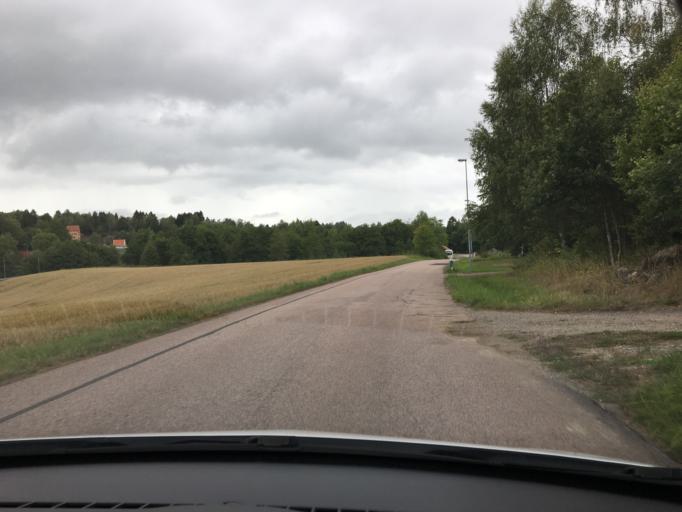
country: SE
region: Vaestra Goetaland
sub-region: Ale Kommun
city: Alafors
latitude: 57.9215
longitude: 12.0886
